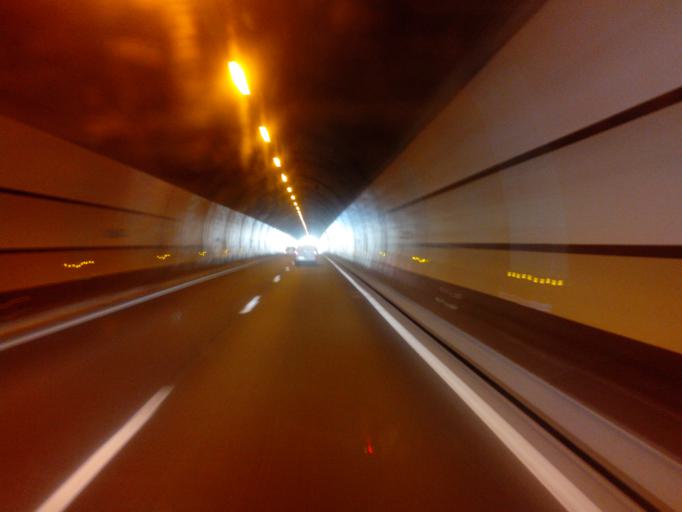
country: FR
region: Limousin
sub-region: Departement de la Correze
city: Brive-la-Gaillarde
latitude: 45.1016
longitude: 1.5188
